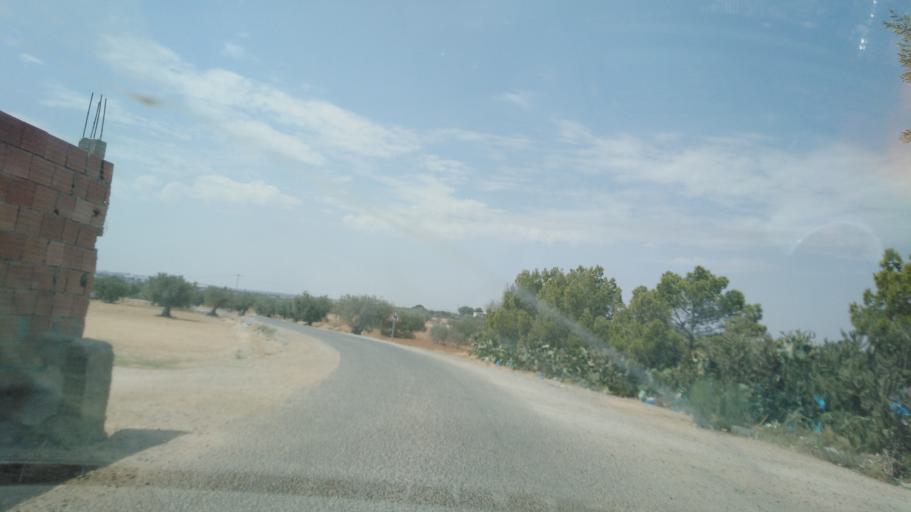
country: TN
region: Safaqis
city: Sfax
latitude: 34.7481
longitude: 10.5563
